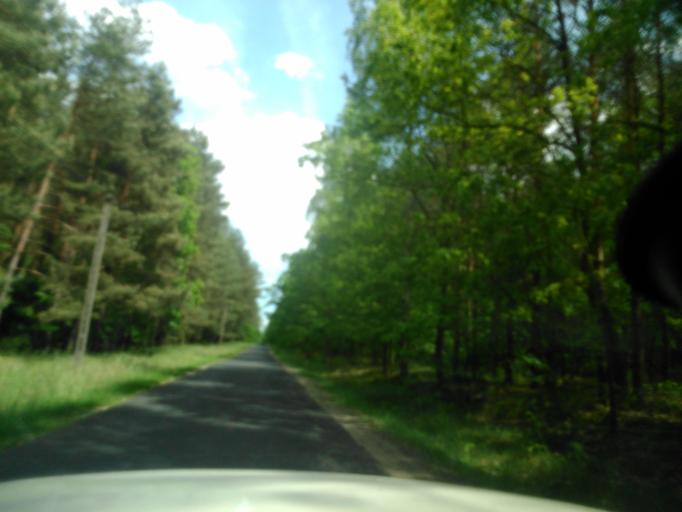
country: PL
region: Kujawsko-Pomorskie
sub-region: Powiat golubsko-dobrzynski
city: Golub-Dobrzyn
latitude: 53.1414
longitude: 19.1170
